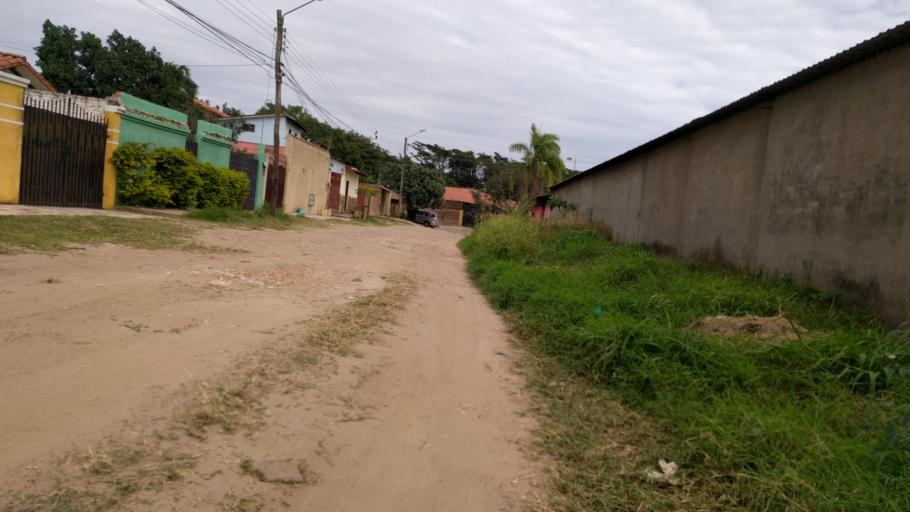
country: BO
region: Santa Cruz
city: Santa Cruz de la Sierra
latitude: -17.8061
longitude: -63.2271
